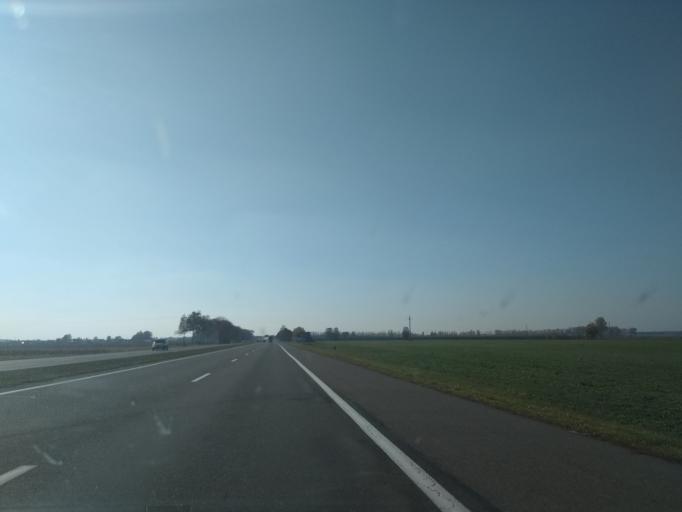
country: BY
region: Brest
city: Zhabinka
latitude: 52.1590
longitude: 24.0693
